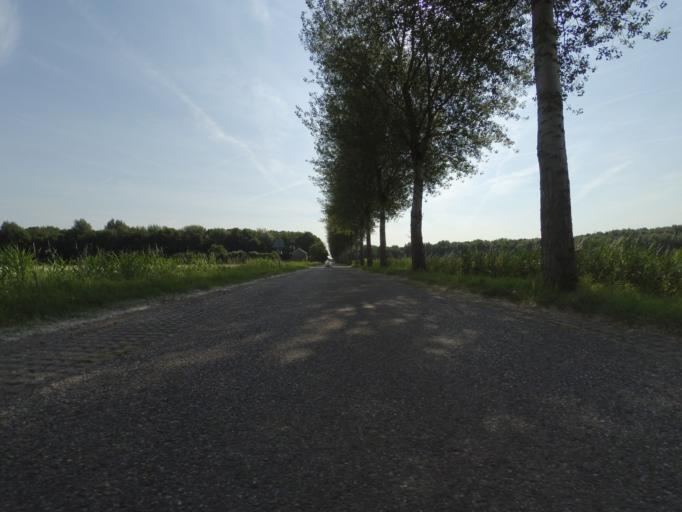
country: NL
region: North Brabant
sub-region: Gemeente Steenbergen
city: Steenbergen
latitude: 51.5739
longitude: 4.3005
